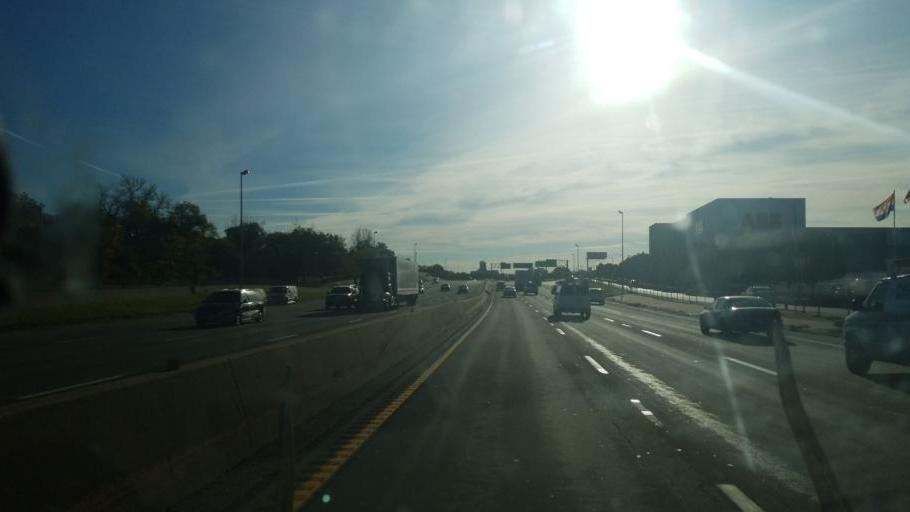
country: US
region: Missouri
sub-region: Saint Louis County
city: Pine Lawn
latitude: 38.6908
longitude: -90.2565
